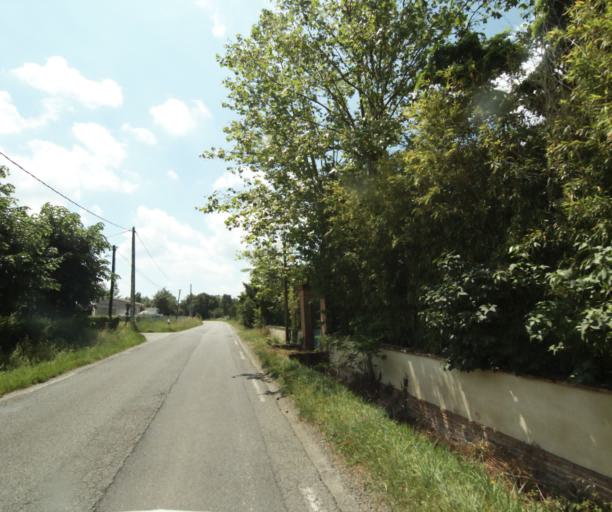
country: FR
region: Midi-Pyrenees
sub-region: Departement du Tarn-et-Garonne
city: Montauban
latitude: 44.0487
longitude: 1.3439
